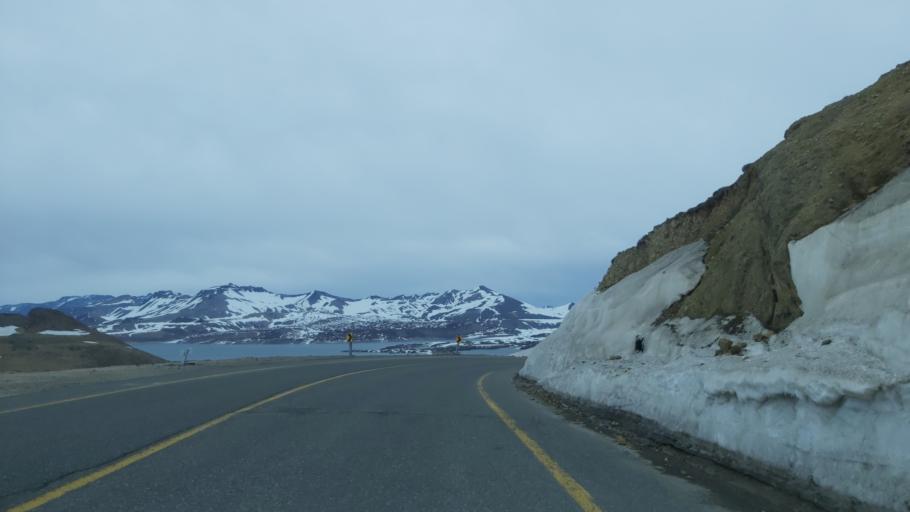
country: CL
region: Maule
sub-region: Provincia de Linares
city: Colbun
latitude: -36.0199
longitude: -70.4992
